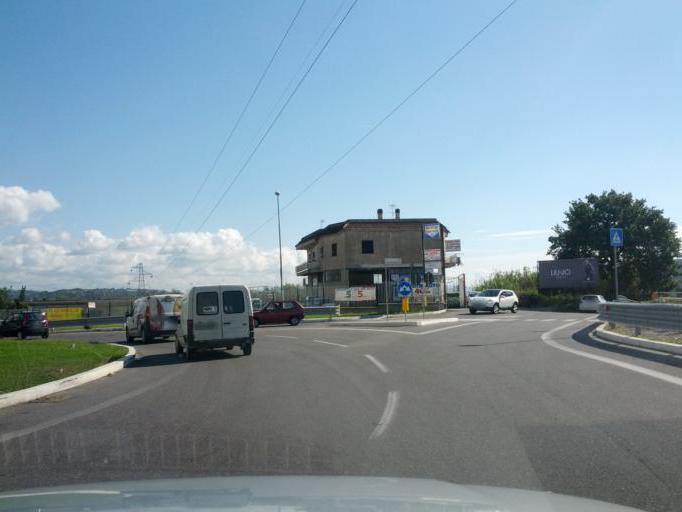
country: IT
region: Latium
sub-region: Provincia di Latina
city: Penitro
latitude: 41.2682
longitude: 13.6726
